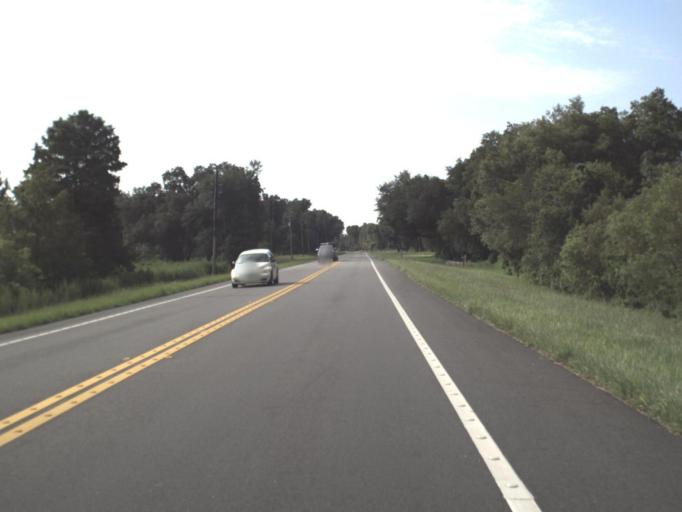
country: US
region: Florida
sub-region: Pasco County
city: Lacoochee
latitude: 28.4614
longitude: -82.1918
